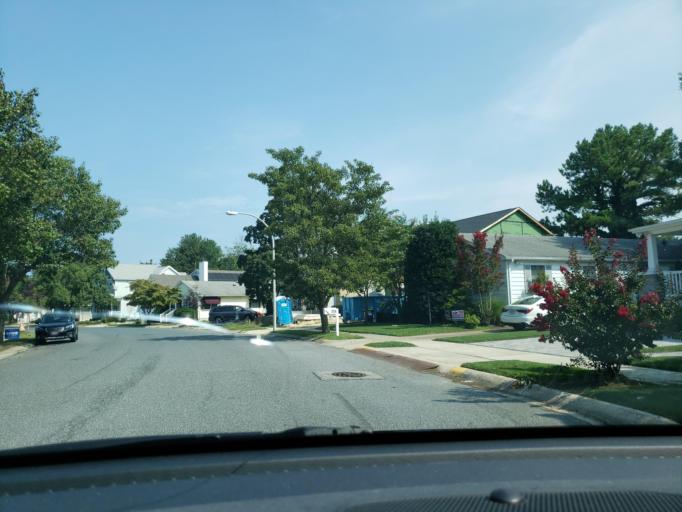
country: US
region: Delaware
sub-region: Sussex County
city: Rehoboth Beach
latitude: 38.7133
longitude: -75.0889
